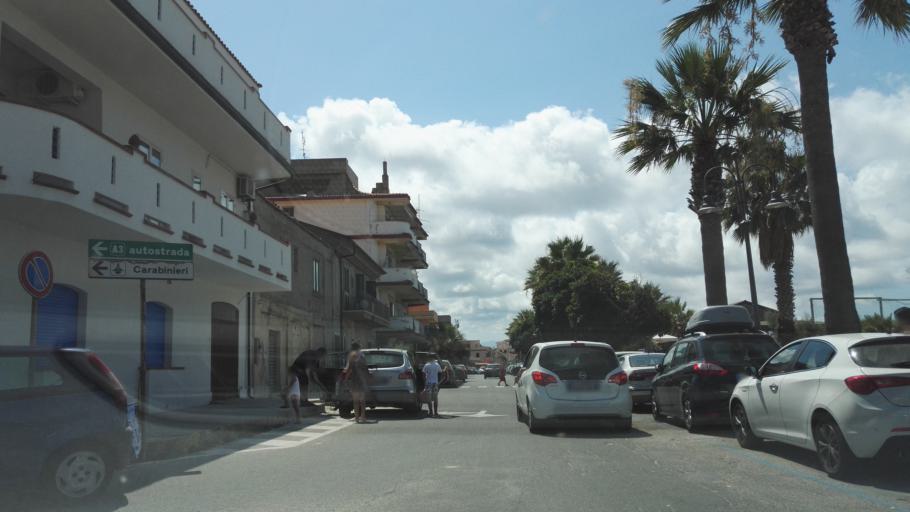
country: IT
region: Calabria
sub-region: Provincia di Vibo-Valentia
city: Nicotera
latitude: 38.5458
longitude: 15.9319
